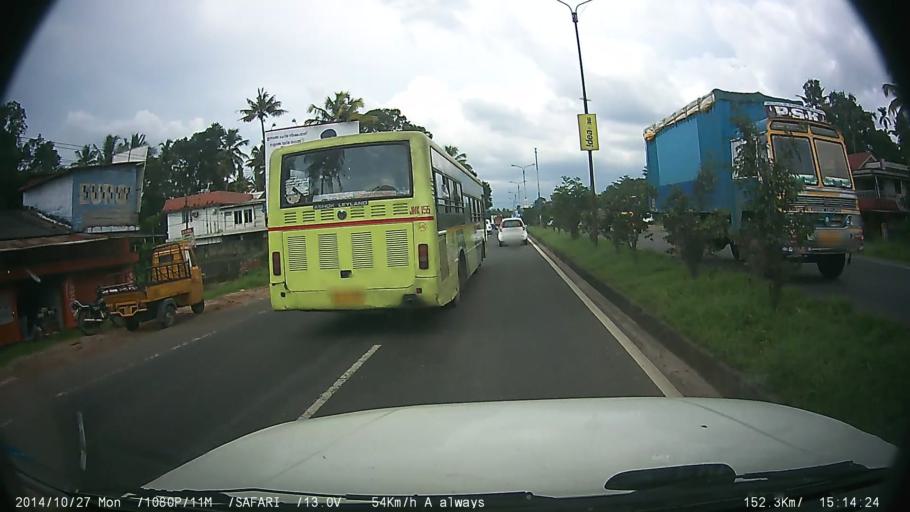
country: IN
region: Kerala
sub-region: Ernakulam
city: Aluva
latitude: 10.1452
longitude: 76.3530
